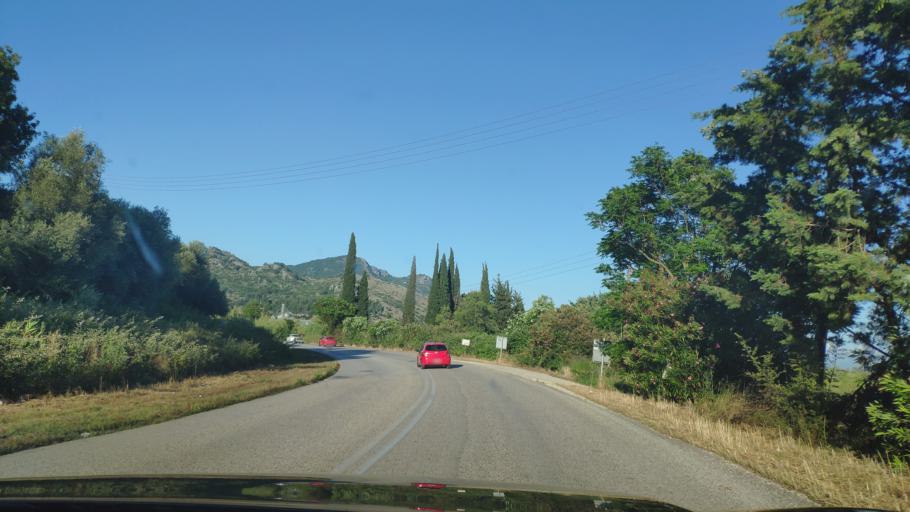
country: GR
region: Epirus
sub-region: Nomos Prevezis
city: Louros
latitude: 39.1760
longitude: 20.7712
